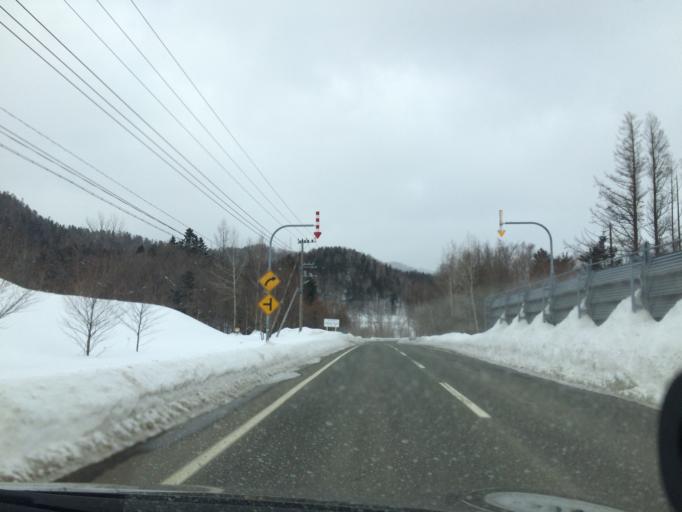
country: JP
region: Hokkaido
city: Shimo-furano
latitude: 43.0576
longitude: 142.5307
